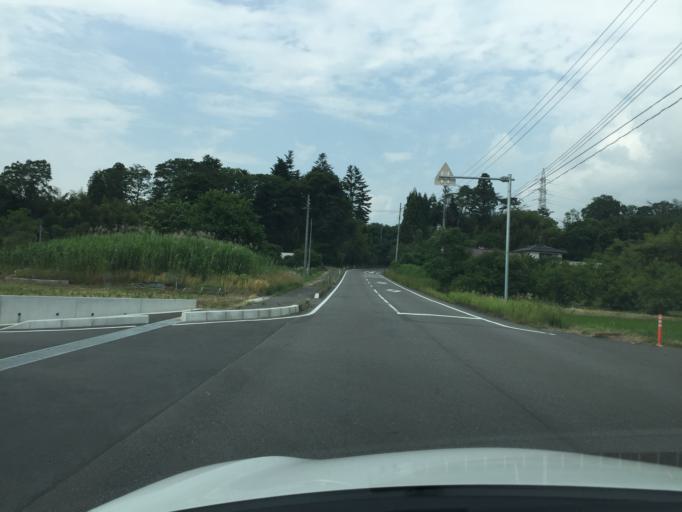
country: JP
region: Fukushima
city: Sukagawa
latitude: 37.2903
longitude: 140.4270
